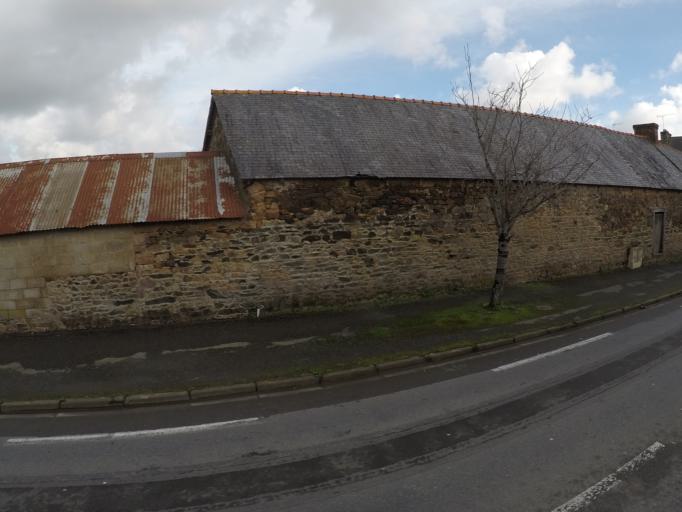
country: FR
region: Brittany
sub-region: Departement des Cotes-d'Armor
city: Lanvollon
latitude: 48.6327
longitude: -2.9878
